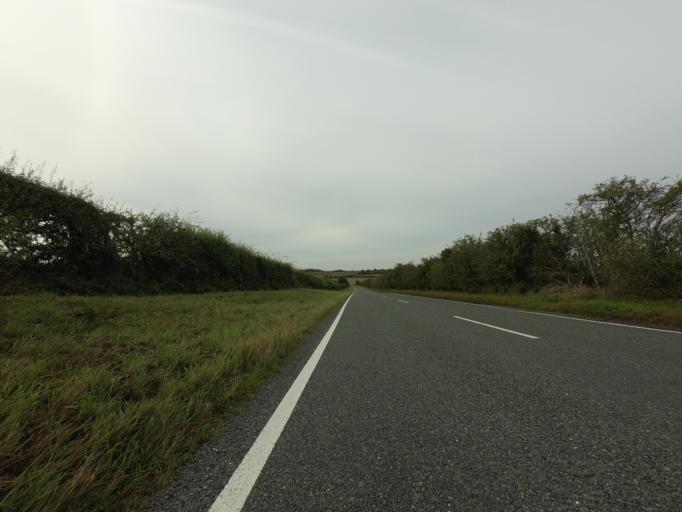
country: GB
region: England
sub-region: Cambridgeshire
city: Melbourn
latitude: 52.0432
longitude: 0.0445
